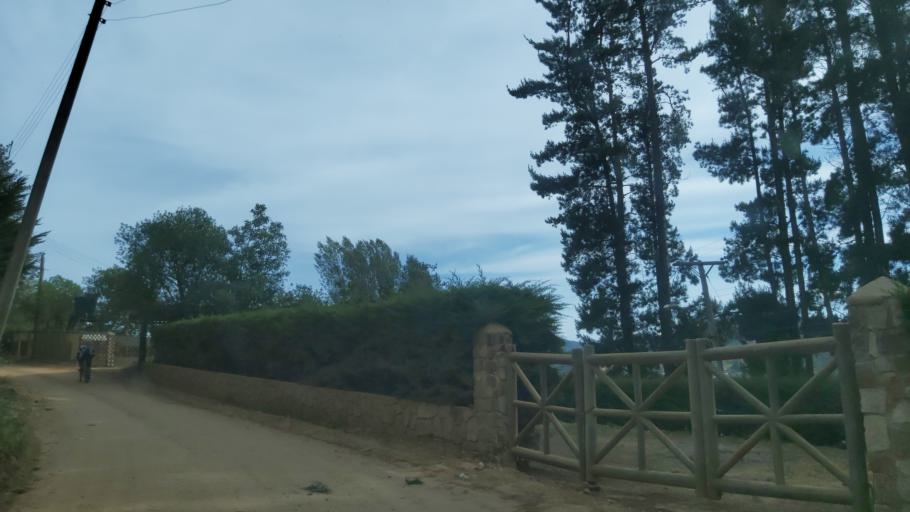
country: CL
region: Maule
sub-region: Provincia de Talca
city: Constitucion
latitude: -34.8433
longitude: -72.0407
